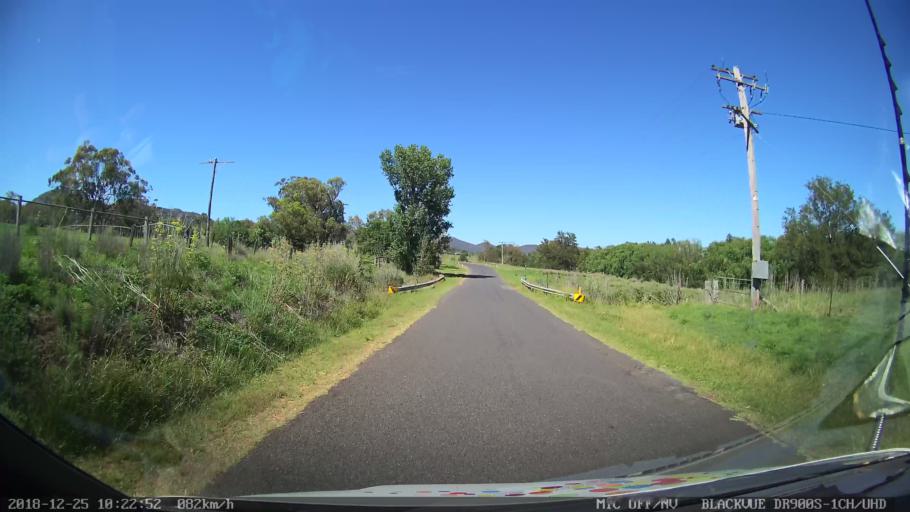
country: AU
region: New South Wales
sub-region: Muswellbrook
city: Denman
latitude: -32.3801
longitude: 150.5274
